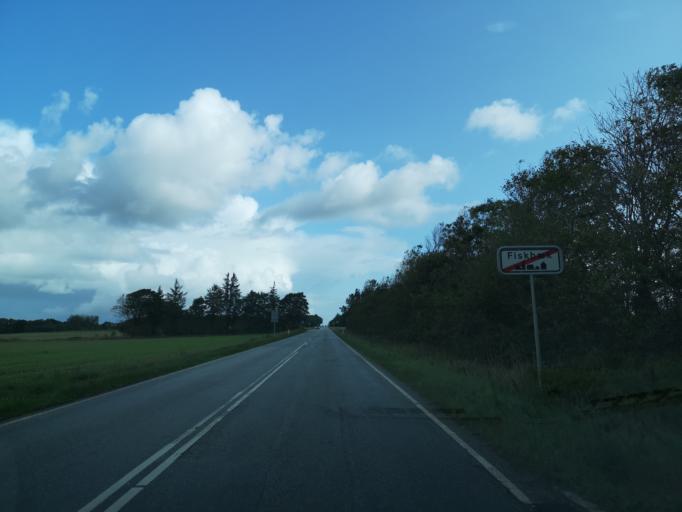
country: DK
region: Central Jutland
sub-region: Ringkobing-Skjern Kommune
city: Videbaek
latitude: 56.0472
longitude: 8.6222
